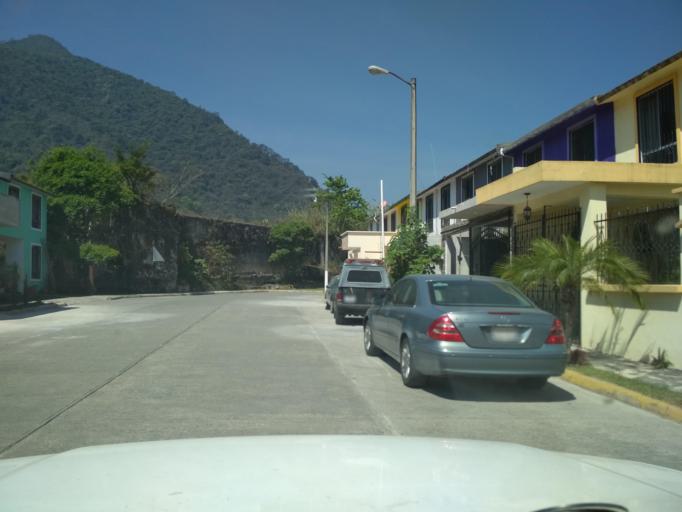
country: MX
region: Veracruz
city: Jalapilla
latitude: 18.8222
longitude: -97.0912
